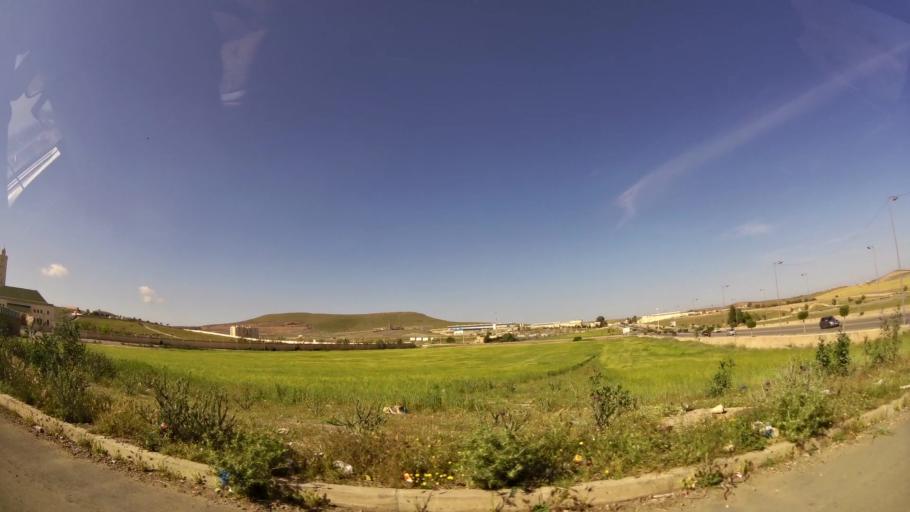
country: MA
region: Oriental
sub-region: Oujda-Angad
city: Oujda
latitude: 34.6568
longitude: -1.9543
